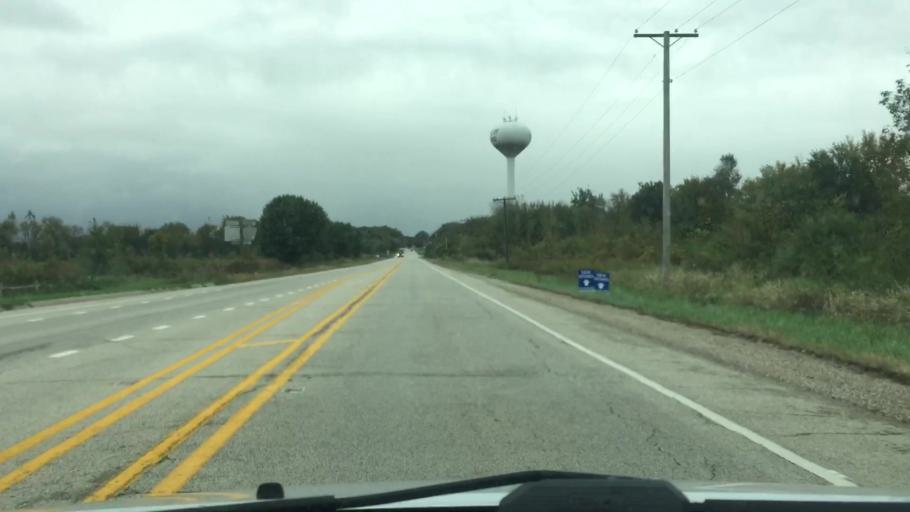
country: US
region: Illinois
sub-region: McHenry County
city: Richmond
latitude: 42.4495
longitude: -88.3059
